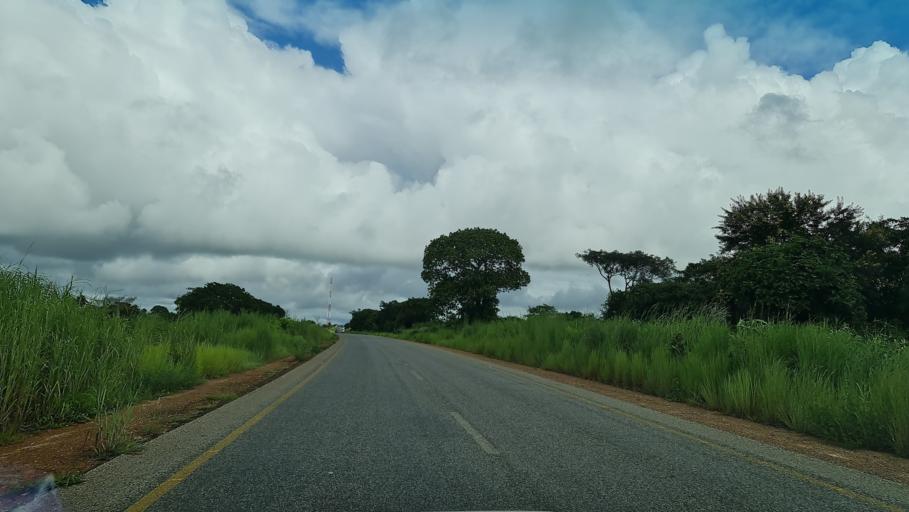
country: MZ
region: Nampula
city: Nampula
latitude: -15.0310
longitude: 38.4452
